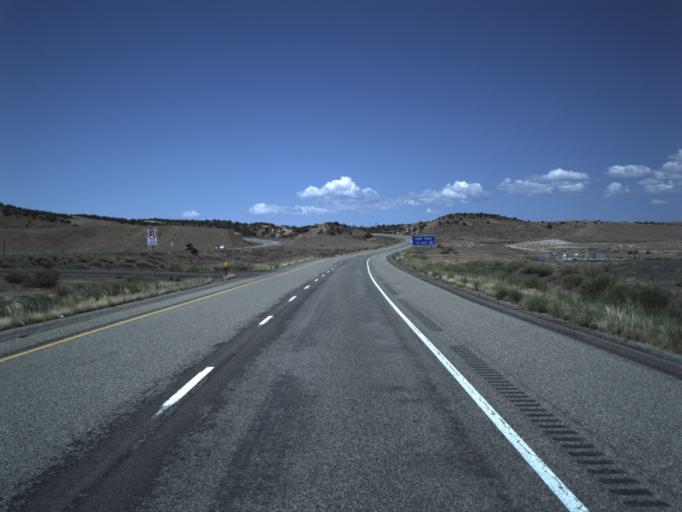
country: US
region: Colorado
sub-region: Mesa County
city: Loma
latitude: 39.1898
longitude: -109.1000
